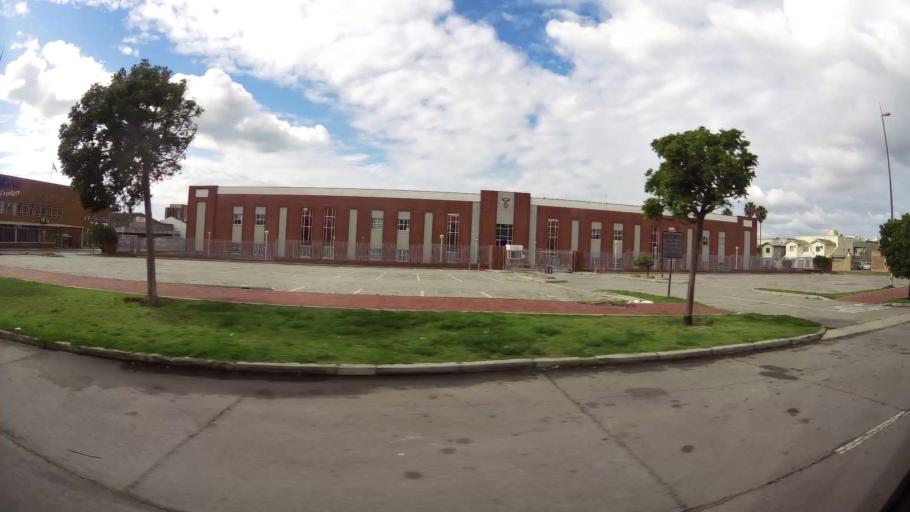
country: ZA
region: Eastern Cape
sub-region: Nelson Mandela Bay Metropolitan Municipality
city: Port Elizabeth
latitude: -33.9443
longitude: 25.6030
